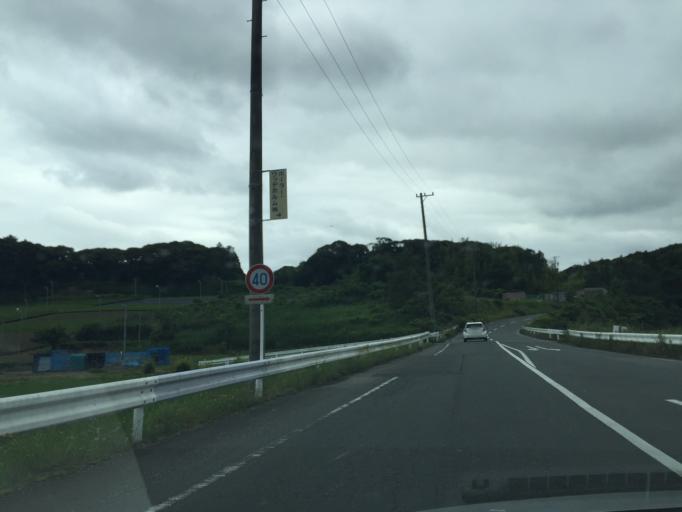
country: JP
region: Shizuoka
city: Fukuroi
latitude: 34.7746
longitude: 137.9296
